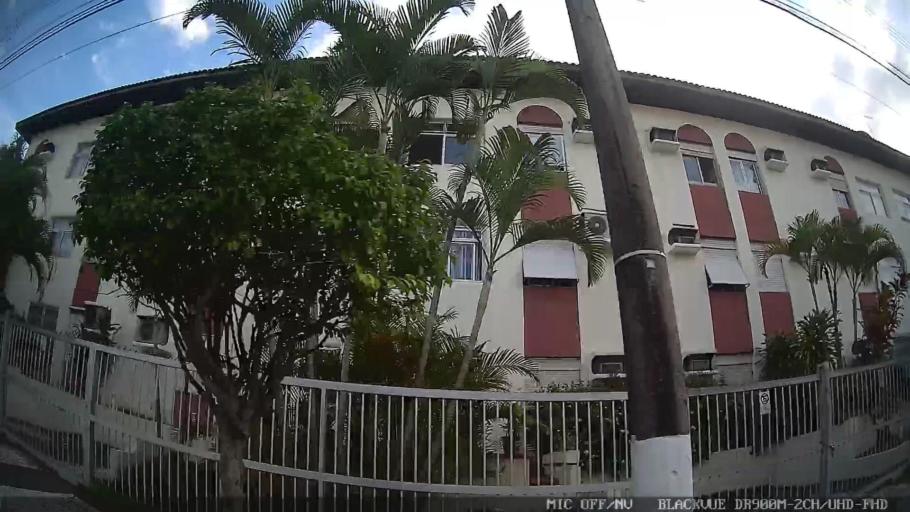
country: BR
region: Sao Paulo
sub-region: Guaruja
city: Guaruja
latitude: -23.9860
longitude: -46.2347
